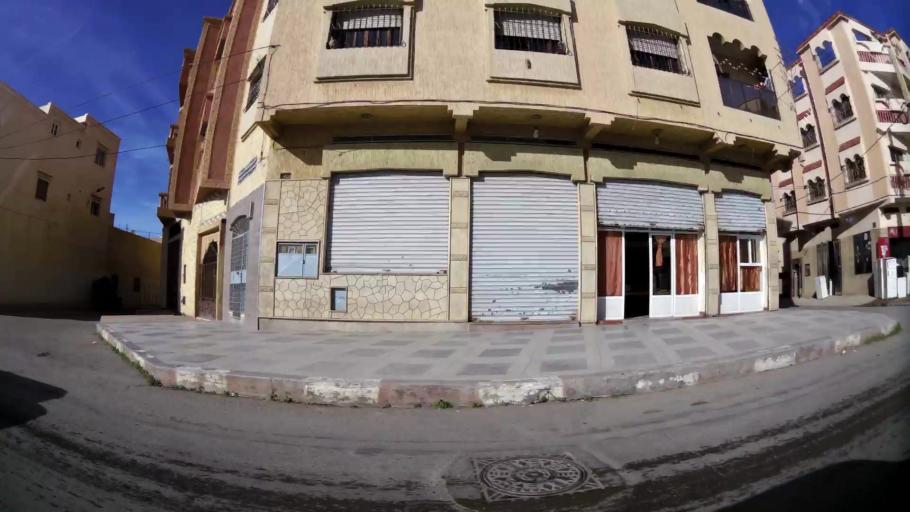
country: MA
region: Oriental
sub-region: Oujda-Angad
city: Oujda
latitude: 34.6717
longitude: -1.8996
